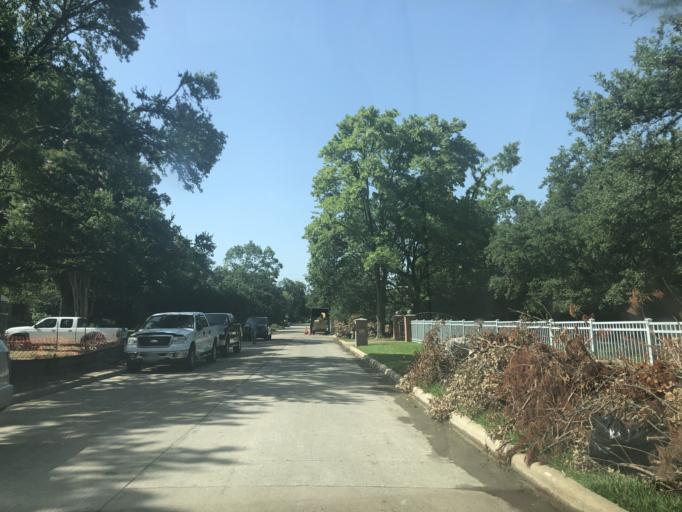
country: US
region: Texas
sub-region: Dallas County
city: University Park
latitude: 32.8817
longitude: -96.8139
